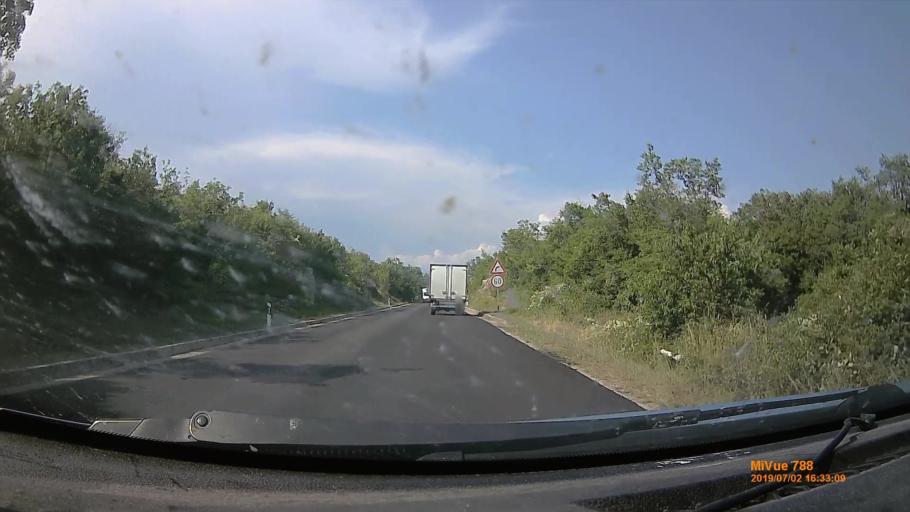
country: HR
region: Primorsko-Goranska
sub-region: Grad Krk
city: Krk
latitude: 45.0718
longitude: 14.4888
